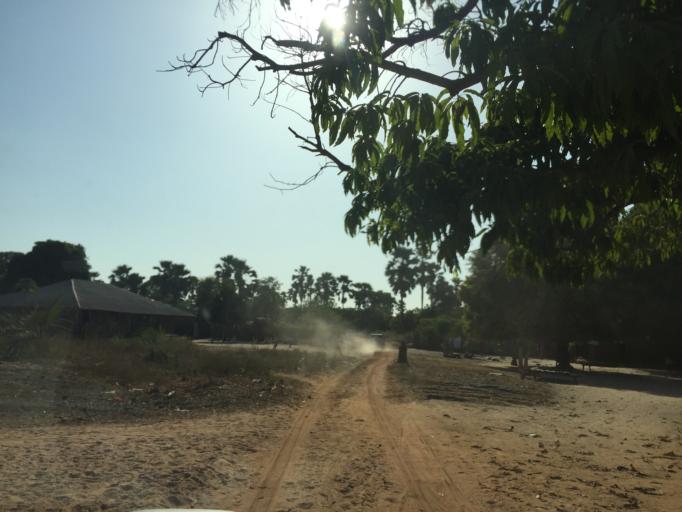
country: GW
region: Oio
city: Farim
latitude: 12.4596
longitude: -15.3046
